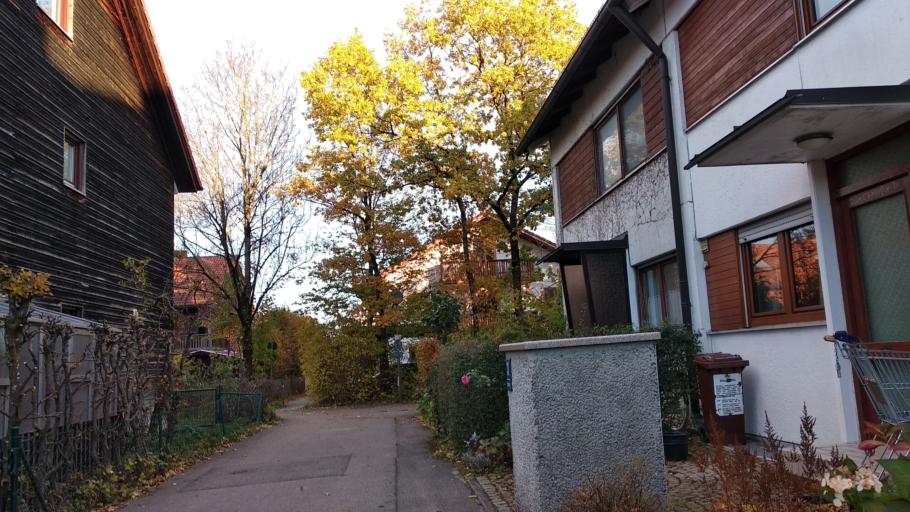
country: DE
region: Bavaria
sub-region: Upper Bavaria
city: Hohenkirchen-Siegertsbrunn
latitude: 48.0192
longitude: 11.7242
